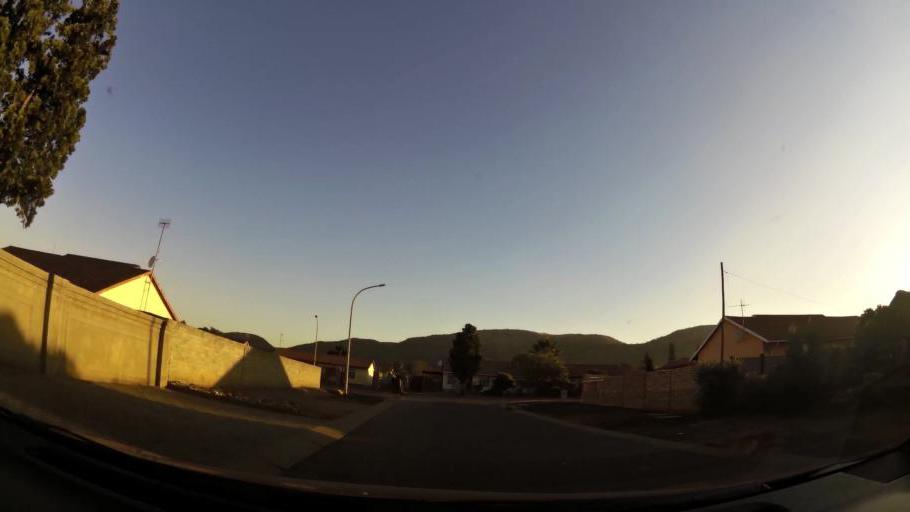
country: ZA
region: North-West
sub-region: Bojanala Platinum District Municipality
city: Rustenburg
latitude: -25.6373
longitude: 27.2053
